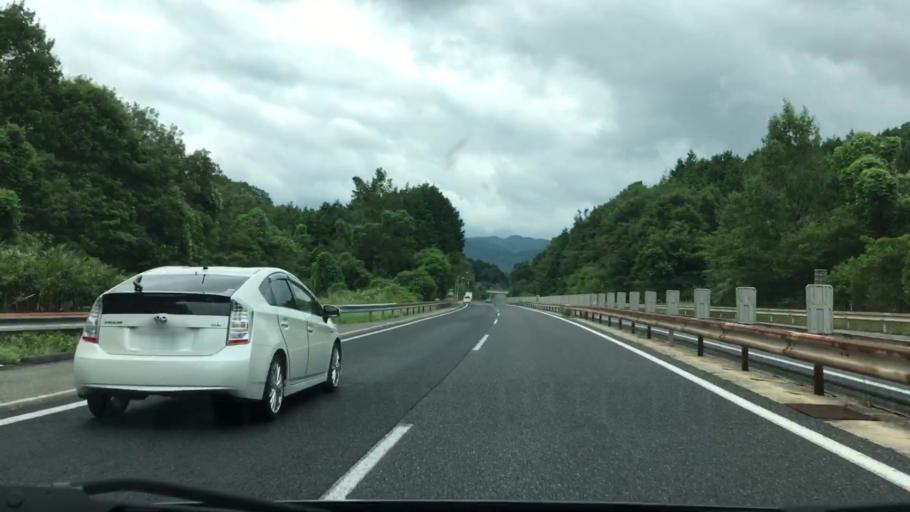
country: JP
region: Okayama
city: Takahashi
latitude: 35.0136
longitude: 133.7297
